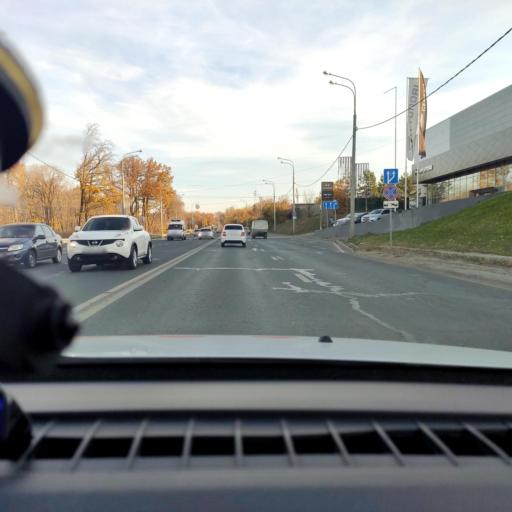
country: RU
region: Samara
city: Samara
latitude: 53.2752
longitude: 50.2268
